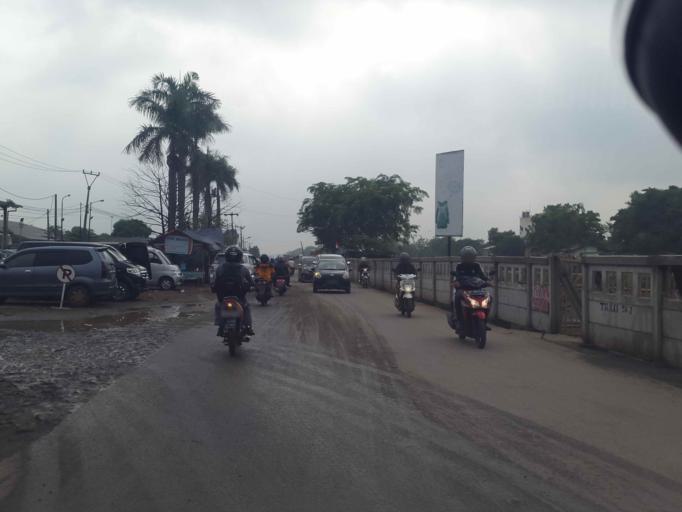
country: ID
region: West Java
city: Cikarang
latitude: -6.2806
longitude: 107.0867
